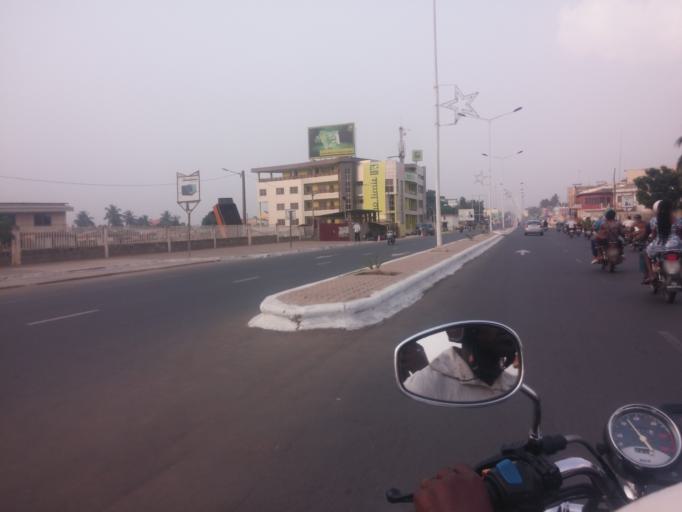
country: TG
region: Maritime
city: Lome
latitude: 6.1528
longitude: 1.2415
